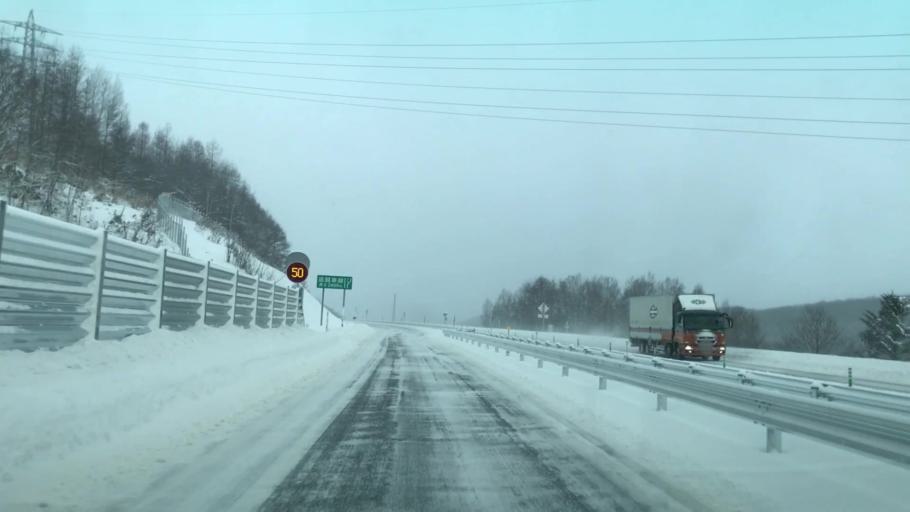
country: JP
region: Hokkaido
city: Otaru
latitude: 43.1986
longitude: 140.9462
